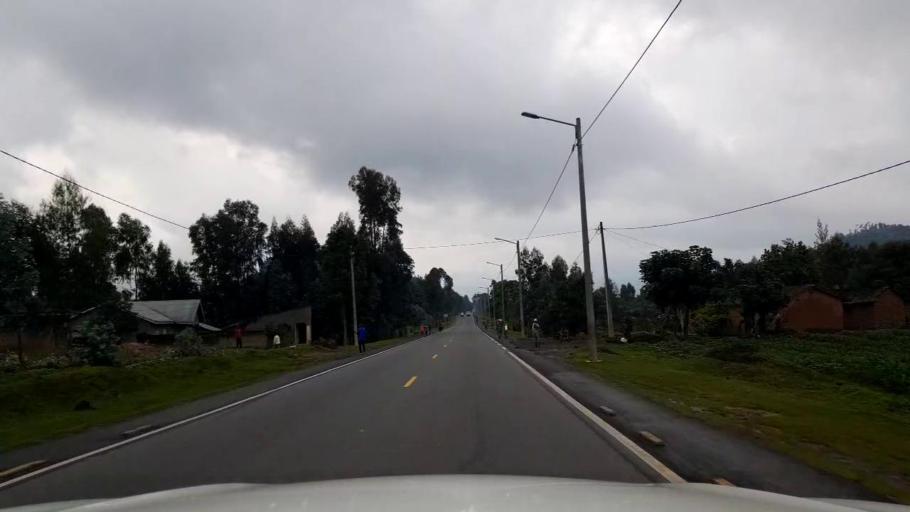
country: RW
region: Northern Province
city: Musanze
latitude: -1.5454
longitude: 29.5584
